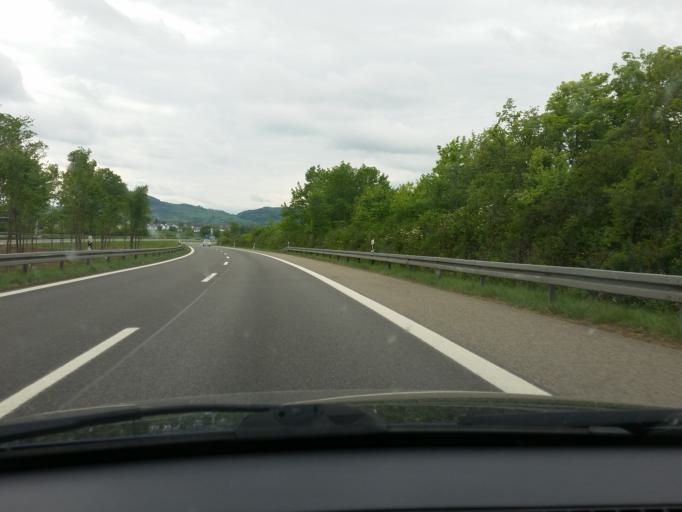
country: DE
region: Baden-Wuerttemberg
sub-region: Freiburg Region
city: Volkertshausen
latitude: 47.8044
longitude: 8.8524
